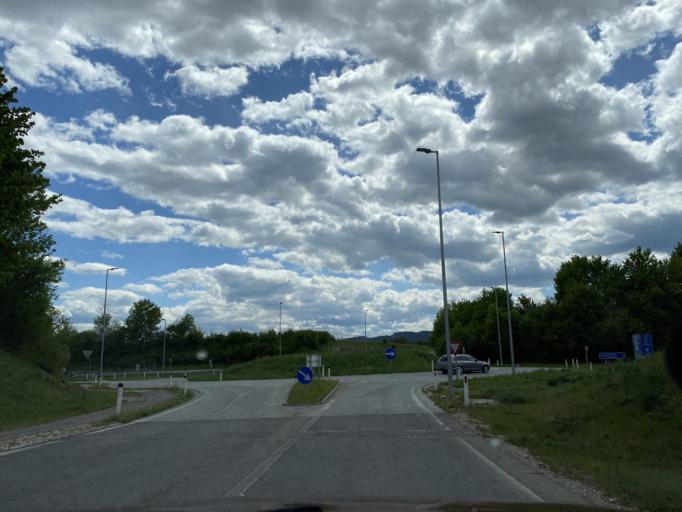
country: AT
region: Carinthia
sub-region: Politischer Bezirk Wolfsberg
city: Wolfsberg
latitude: 46.8240
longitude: 14.8265
